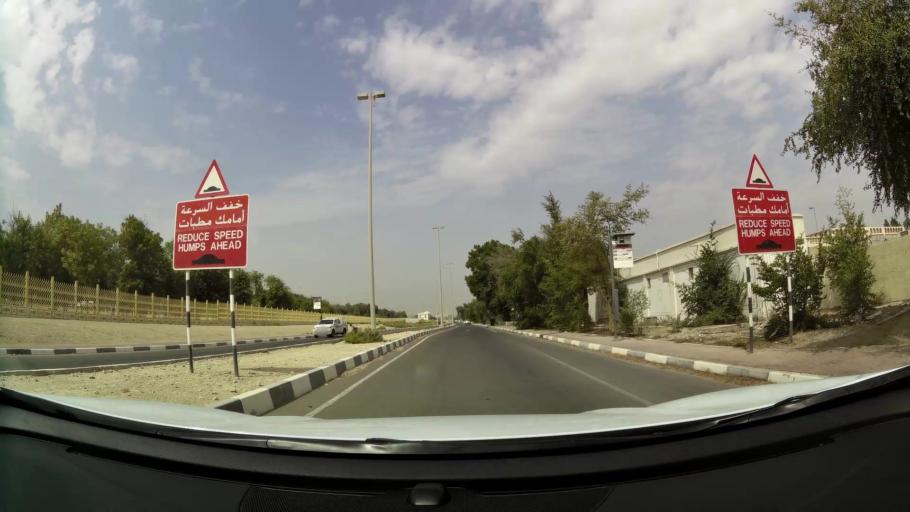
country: AE
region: Abu Dhabi
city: Abu Dhabi
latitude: 24.3002
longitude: 54.6237
